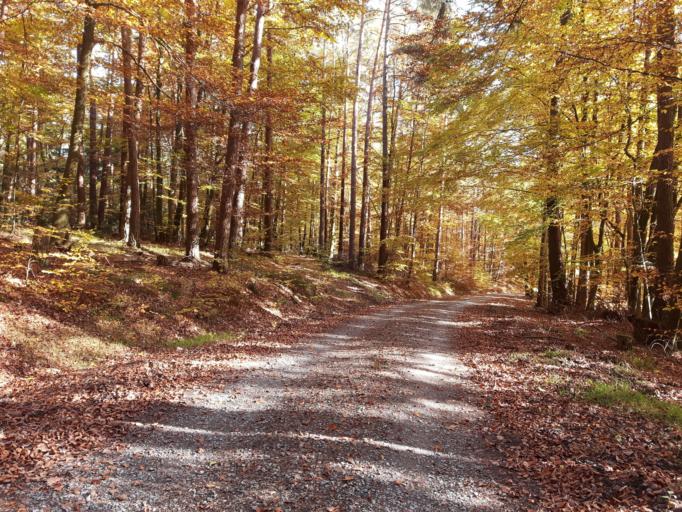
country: DE
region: Bavaria
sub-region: Regierungsbezirk Unterfranken
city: Heimbuchenthal
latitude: 49.8989
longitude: 9.2901
